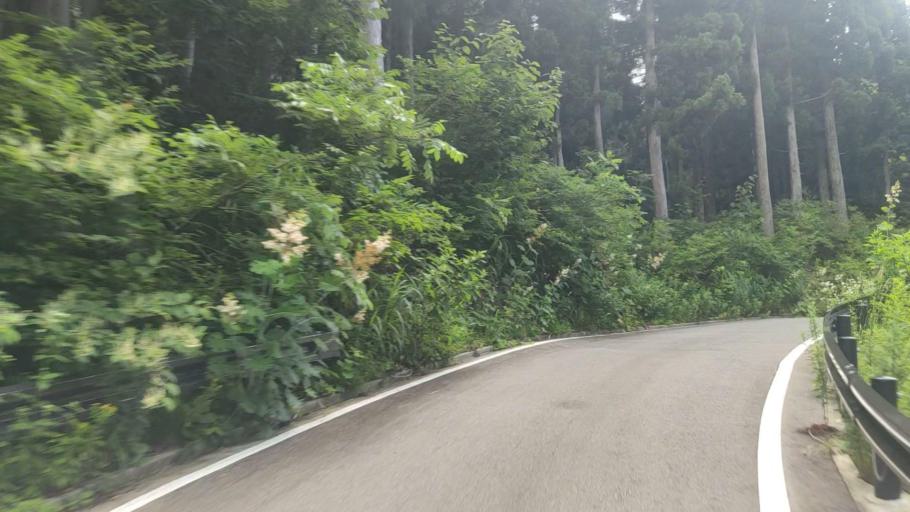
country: JP
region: Fukui
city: Katsuyama
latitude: 36.1621
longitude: 136.5263
